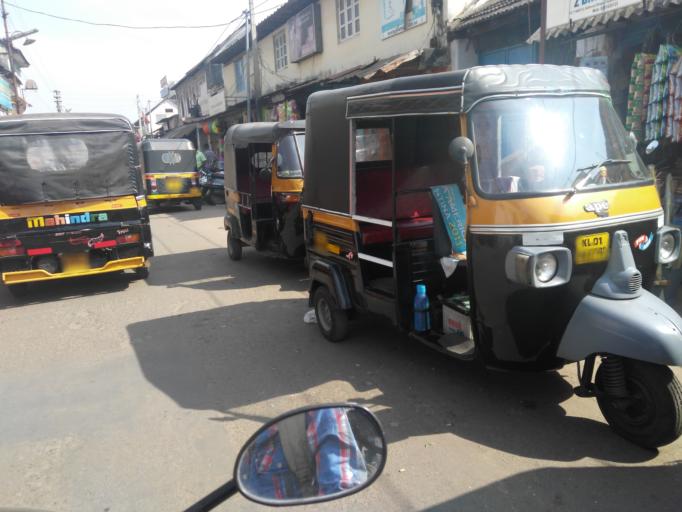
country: IN
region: Kerala
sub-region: Thiruvananthapuram
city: Thiruvananthapuram
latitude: 8.4814
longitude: 76.9506
